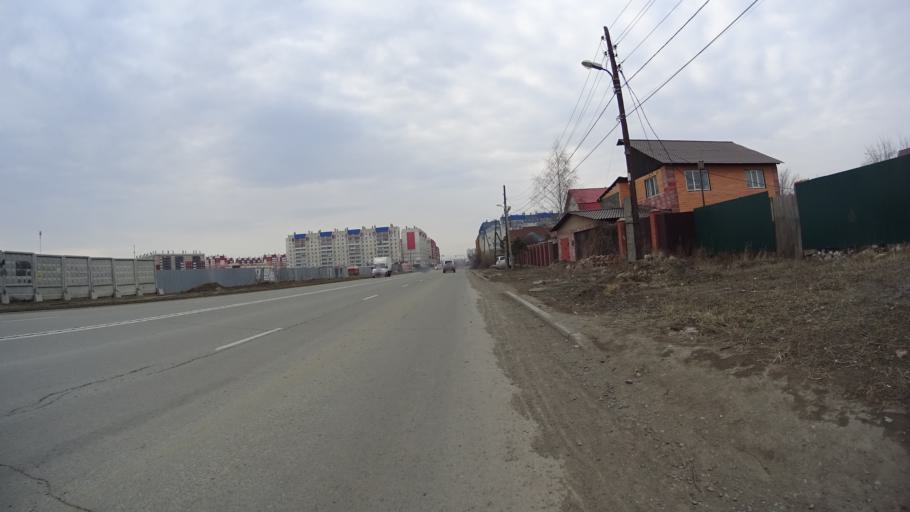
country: RU
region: Chelyabinsk
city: Zheleznodorozhnyy
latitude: 55.1635
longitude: 61.5226
